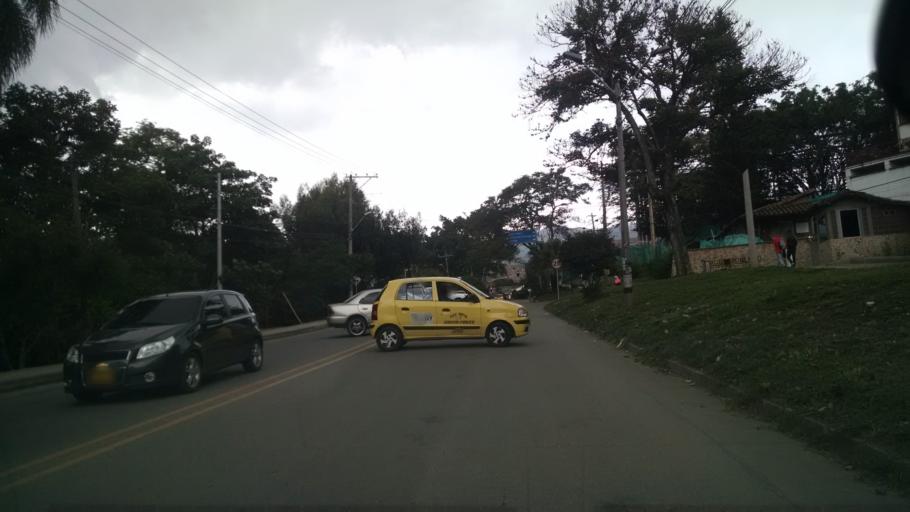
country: CO
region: Antioquia
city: Medellin
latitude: 6.2729
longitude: -75.5895
